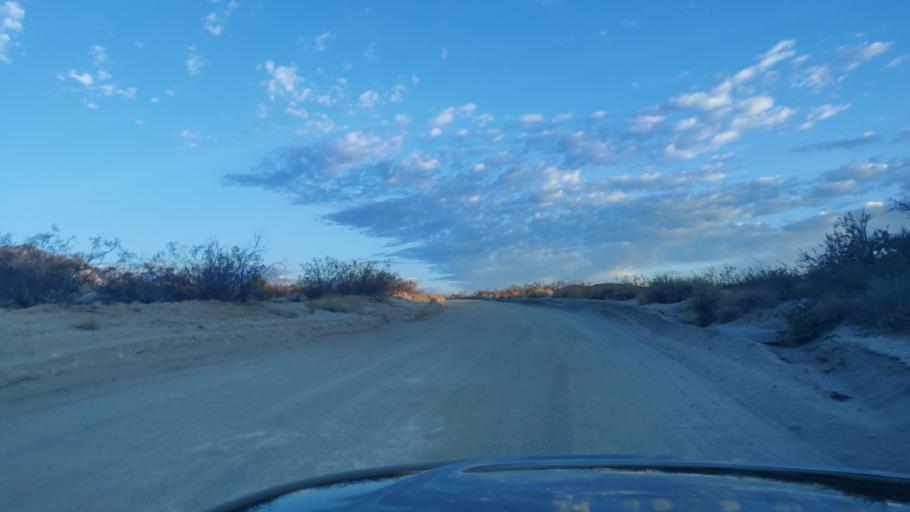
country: US
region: Nevada
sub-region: Clark County
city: Laughlin
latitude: 35.2142
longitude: -114.6750
